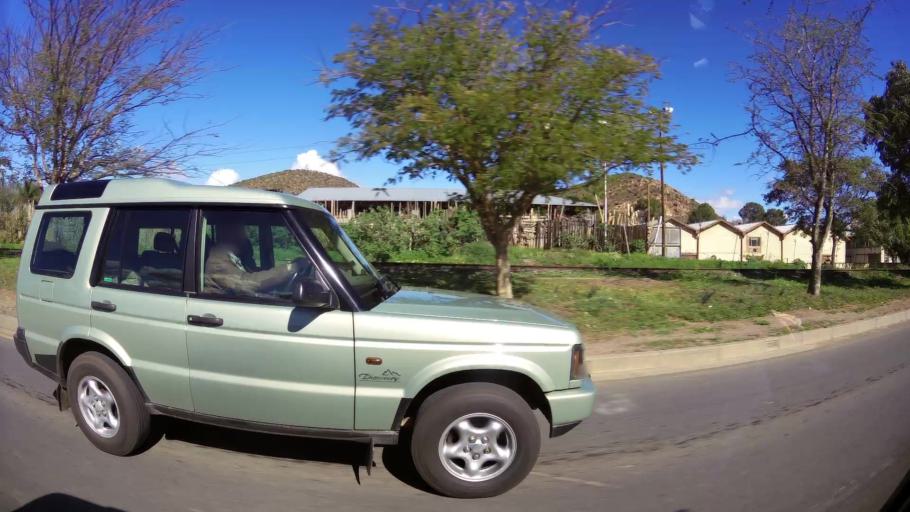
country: ZA
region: Western Cape
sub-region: Cape Winelands District Municipality
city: Ashton
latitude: -33.8124
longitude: 19.8832
